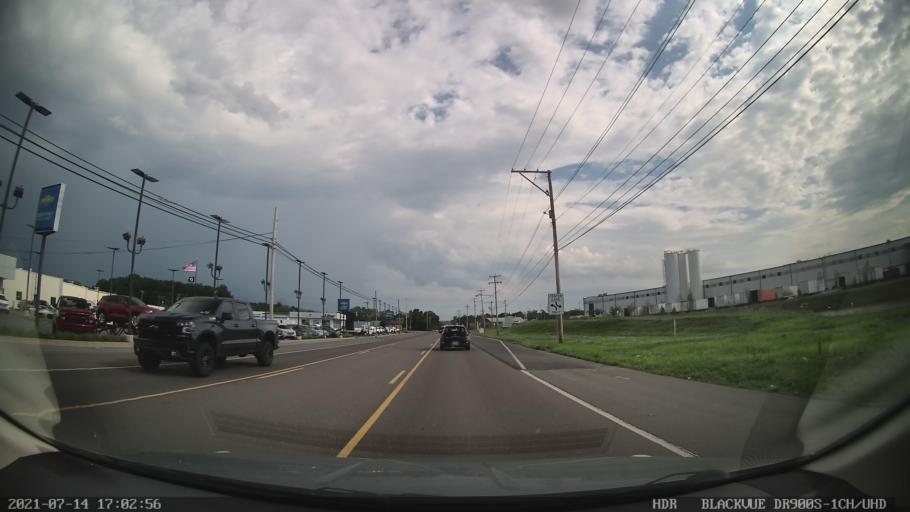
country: US
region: Pennsylvania
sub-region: Berks County
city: Muhlenberg Park
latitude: 40.3978
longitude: -75.9358
